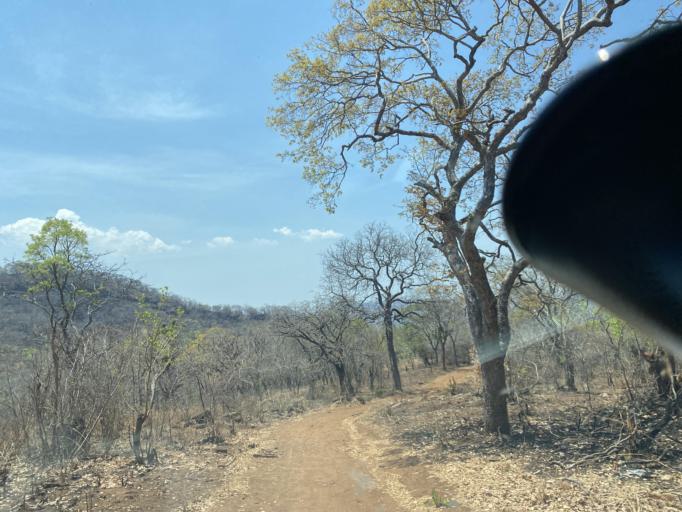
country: ZM
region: Lusaka
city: Kafue
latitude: -15.8042
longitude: 28.4476
